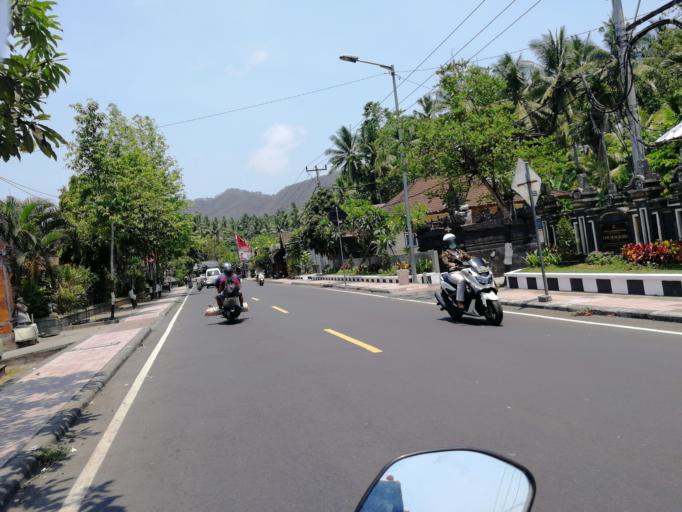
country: ID
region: Bali
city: Banjar Pegeringsingan
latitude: -8.4995
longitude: 115.5538
